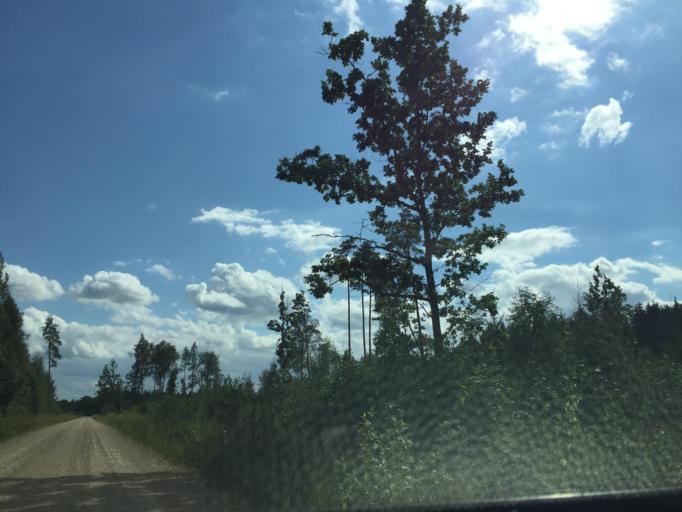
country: LV
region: Kegums
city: Kegums
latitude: 56.8229
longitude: 24.7465
